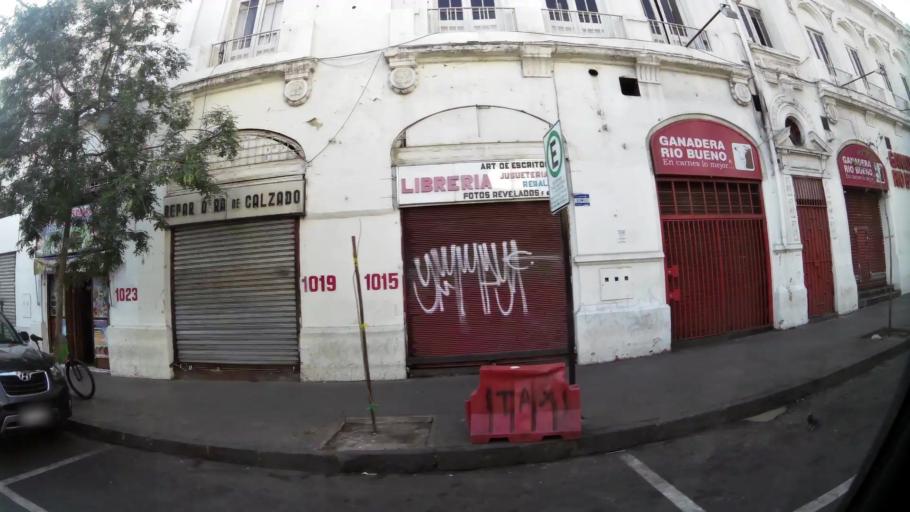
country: CL
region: Santiago Metropolitan
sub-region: Provincia de Santiago
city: Santiago
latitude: -33.4342
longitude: -70.6520
